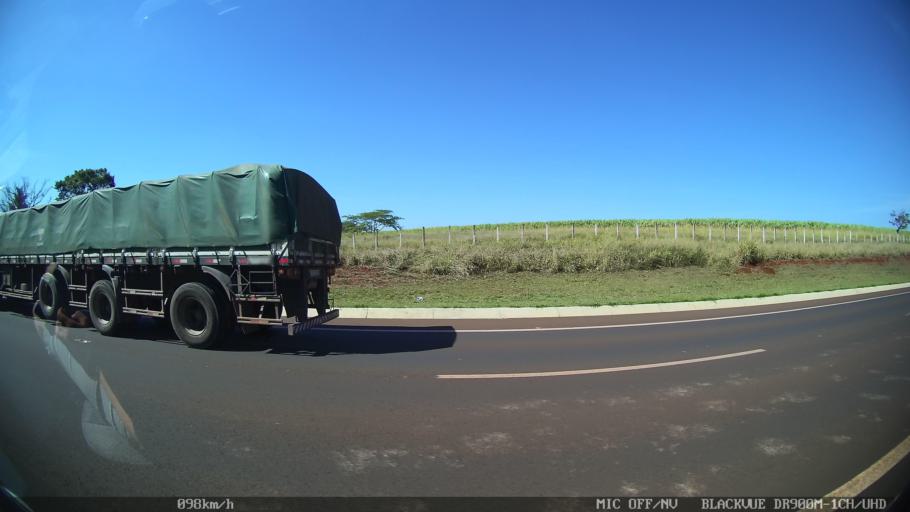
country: BR
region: Sao Paulo
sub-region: Franca
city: Franca
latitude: -20.6577
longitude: -47.4925
